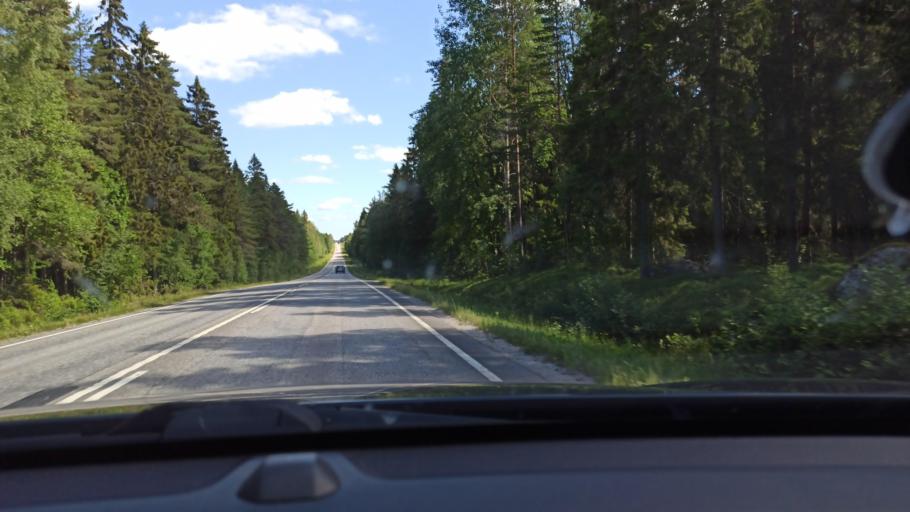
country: FI
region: Ostrobothnia
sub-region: Vaasa
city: Malax
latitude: 62.9882
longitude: 21.6385
